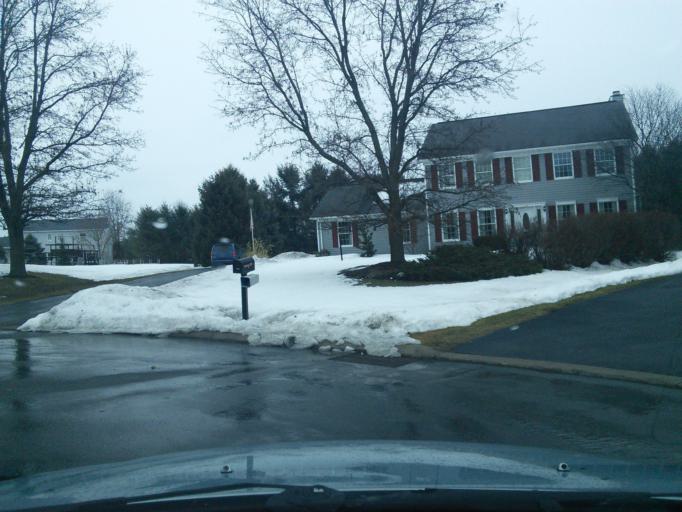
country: US
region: Pennsylvania
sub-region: Centre County
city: State College
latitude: 40.7641
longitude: -77.8736
